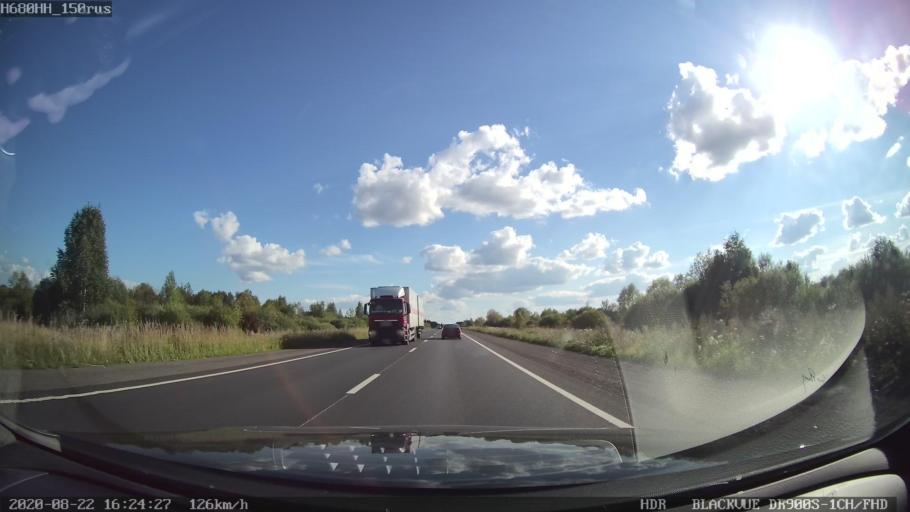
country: RU
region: Tverskaya
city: Rameshki
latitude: 57.3368
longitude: 36.0951
